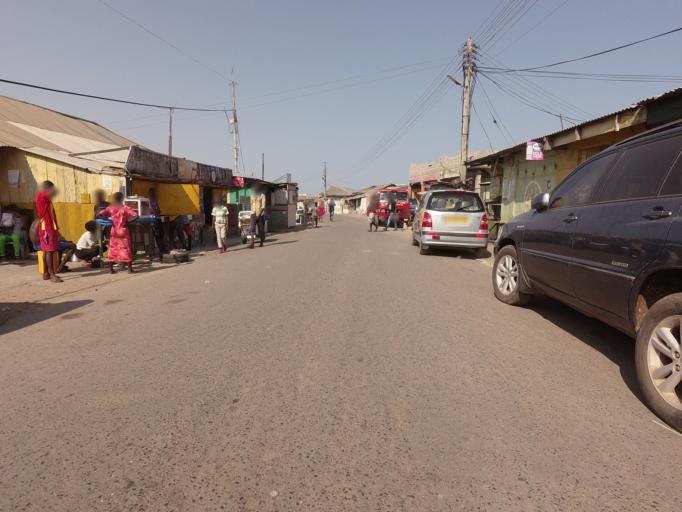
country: GH
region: Greater Accra
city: Teshi Old Town
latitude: 5.5797
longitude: -0.1019
